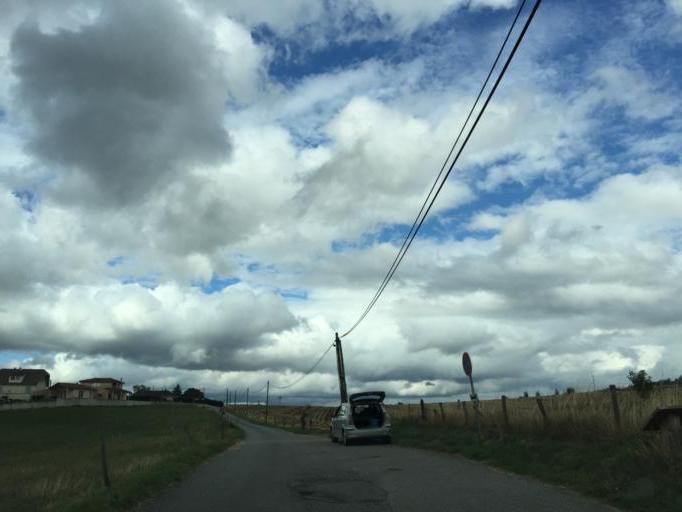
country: FR
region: Rhone-Alpes
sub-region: Departement de la Loire
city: Saint-Paul-en-Jarez
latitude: 45.4714
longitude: 4.5497
